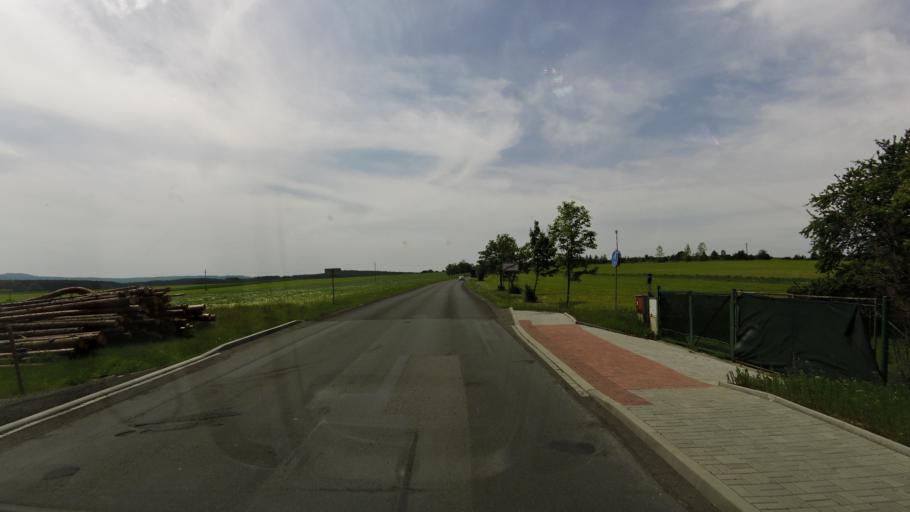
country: CZ
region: Plzensky
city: Zbiroh
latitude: 49.8223
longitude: 13.7764
